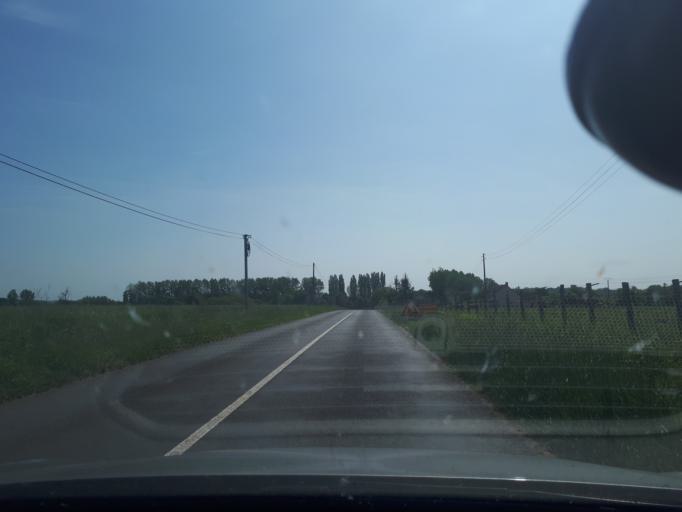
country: FR
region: Pays de la Loire
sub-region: Departement de la Sarthe
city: Champagne
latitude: 48.0810
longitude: 0.3191
